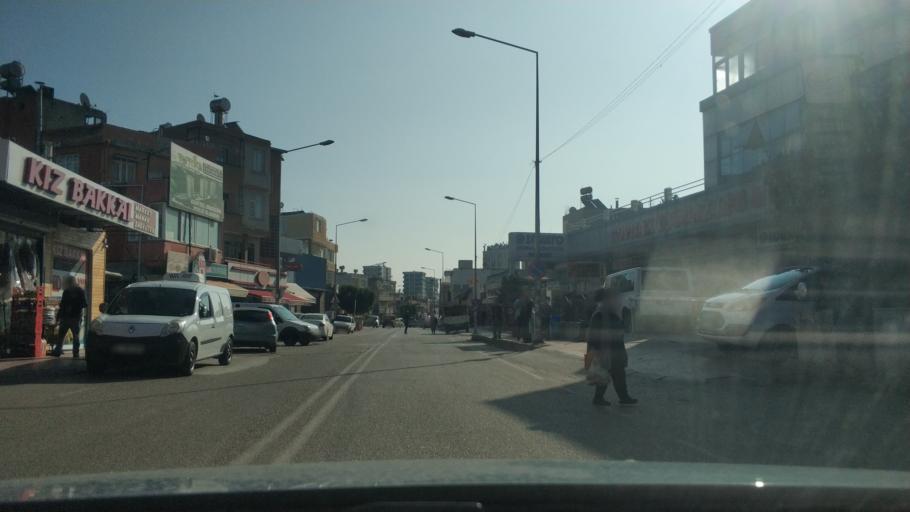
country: TR
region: Adana
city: Seyhan
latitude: 37.0196
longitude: 35.2964
